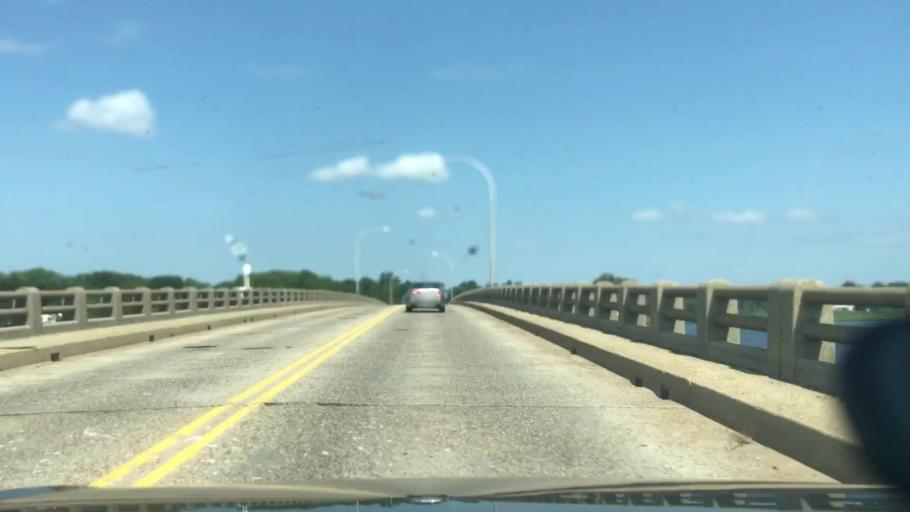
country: US
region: New Jersey
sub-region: Monmouth County
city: Oceanport
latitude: 40.3244
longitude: -74.0190
